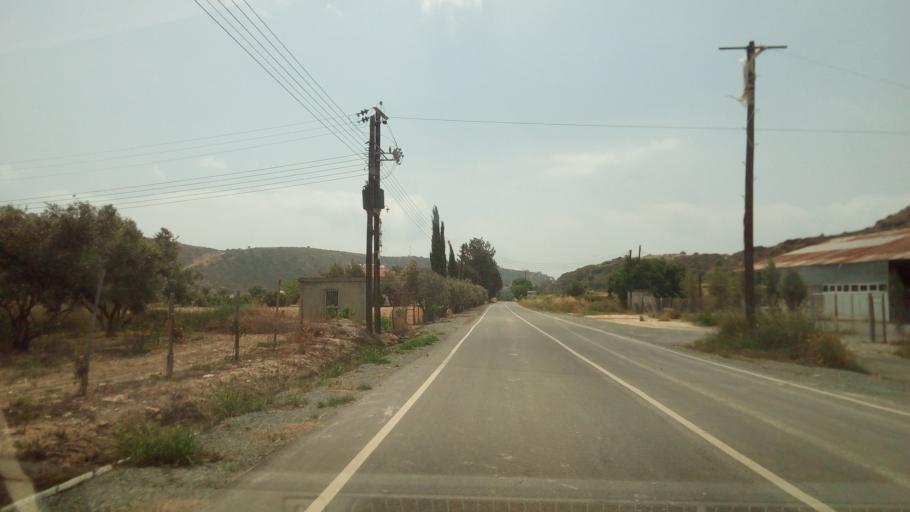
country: CY
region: Limassol
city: Pissouri
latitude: 34.6679
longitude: 32.7265
